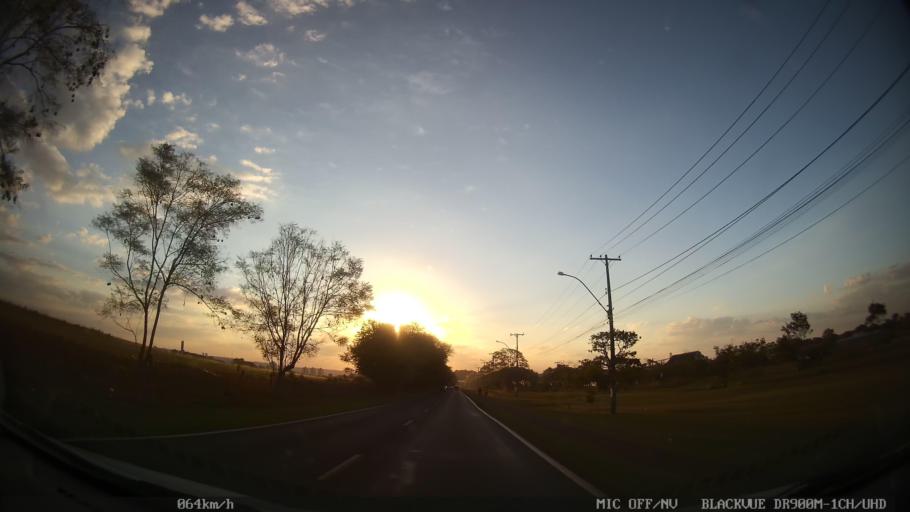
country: BR
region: Sao Paulo
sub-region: Ribeirao Preto
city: Ribeirao Preto
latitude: -21.1574
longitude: -47.7729
